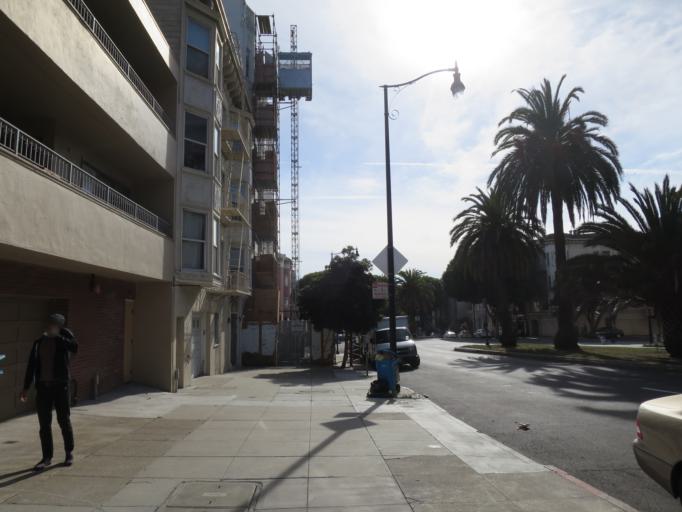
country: US
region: California
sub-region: San Francisco County
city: San Francisco
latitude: 37.7684
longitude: -122.4266
